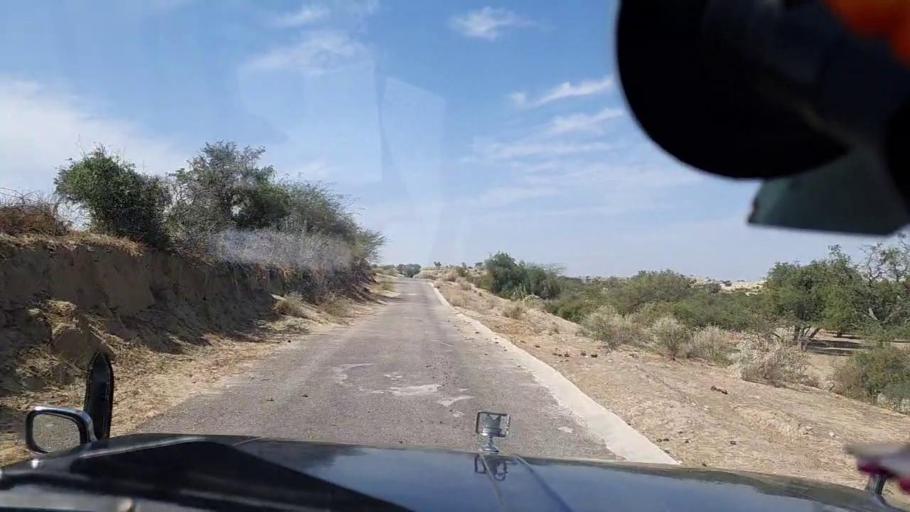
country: PK
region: Sindh
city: Diplo
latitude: 24.3488
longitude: 69.5850
